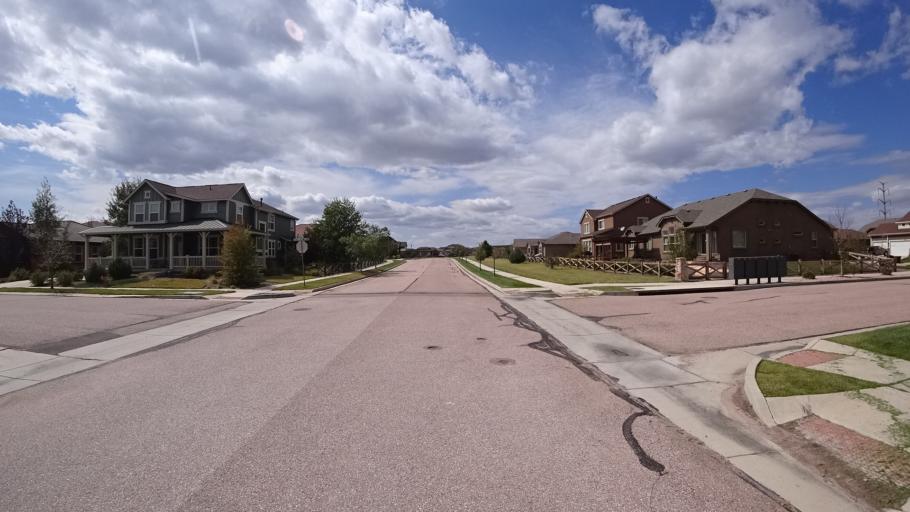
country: US
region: Colorado
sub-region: El Paso County
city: Cimarron Hills
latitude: 38.9357
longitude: -104.6744
